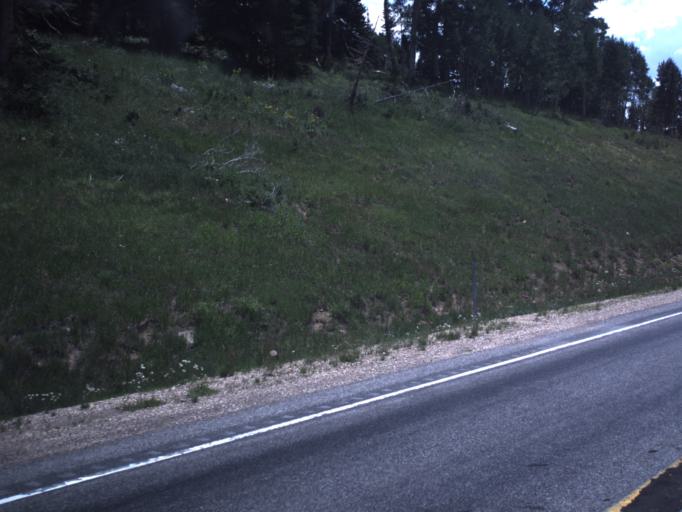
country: US
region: Utah
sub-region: Sanpete County
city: Fairview
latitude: 39.6112
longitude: -111.2805
